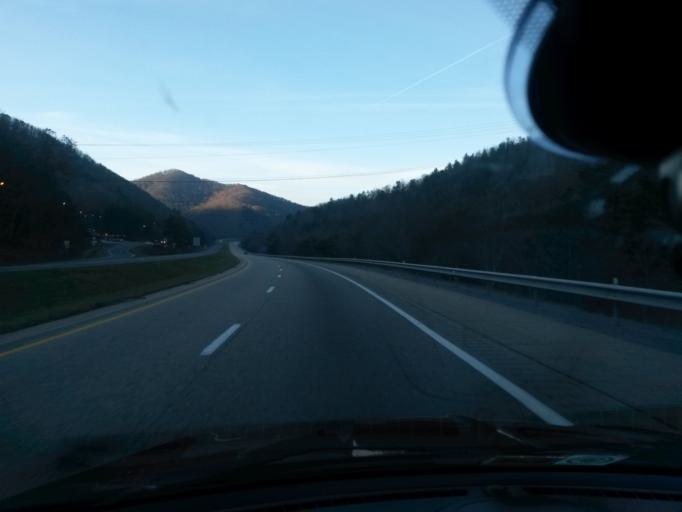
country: US
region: West Virginia
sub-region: Greenbrier County
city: White Sulphur Springs
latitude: 37.8131
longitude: -80.1874
